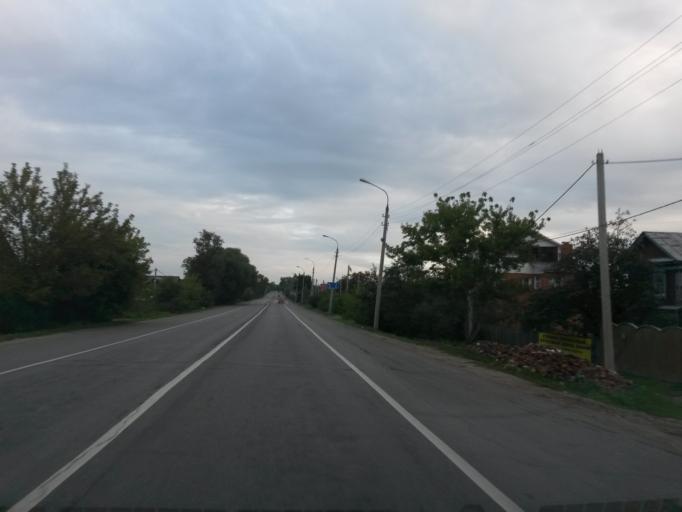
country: RU
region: Moskovskaya
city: Stolbovaya
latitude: 55.2774
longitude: 37.5100
